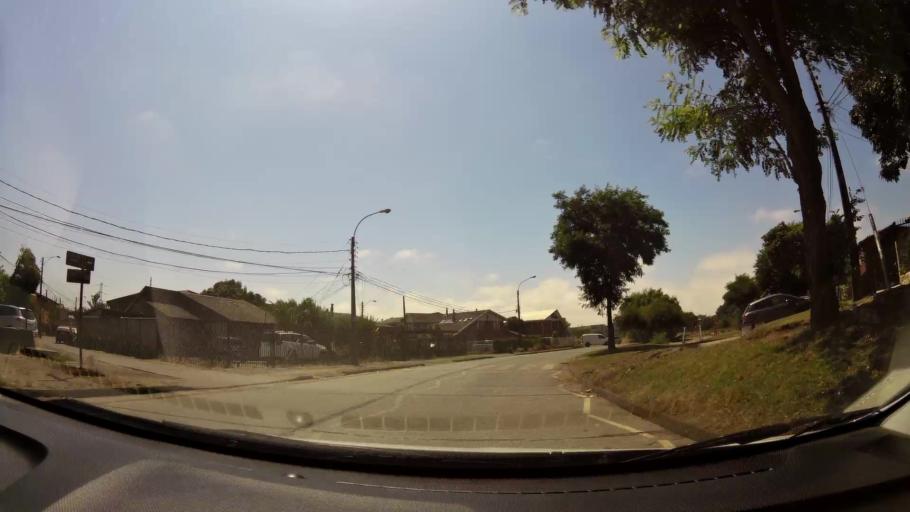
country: CL
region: Biobio
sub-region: Provincia de Concepcion
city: Concepcion
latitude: -36.8059
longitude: -73.0737
